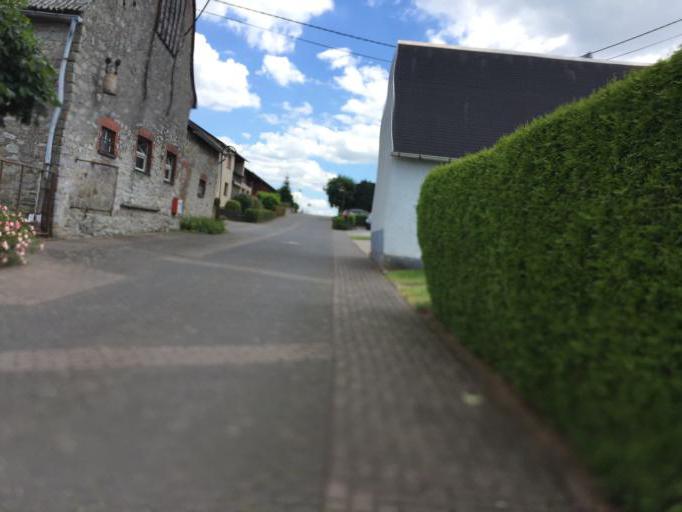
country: DE
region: Rheinland-Pfalz
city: Ruppach-Goldhausen
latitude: 50.4782
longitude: 7.9012
